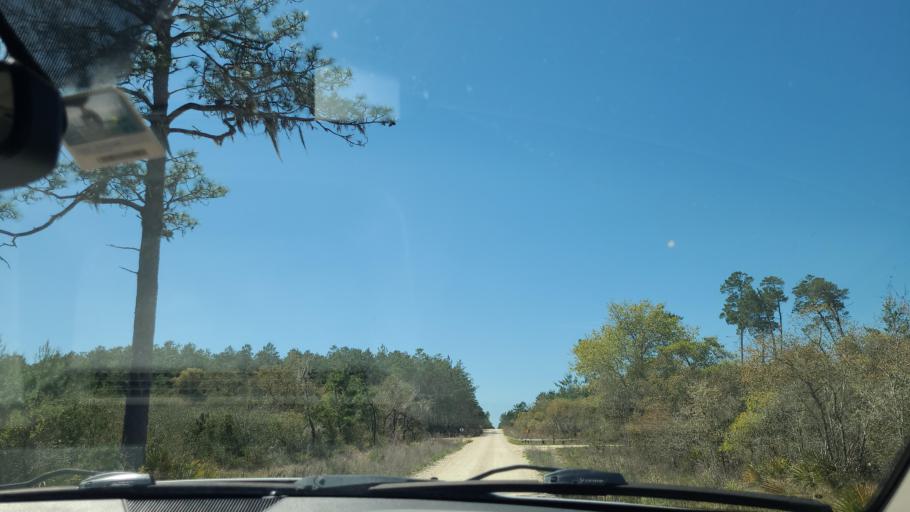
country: US
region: Florida
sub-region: Putnam County
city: Interlachen
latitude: 29.4287
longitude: -81.8235
